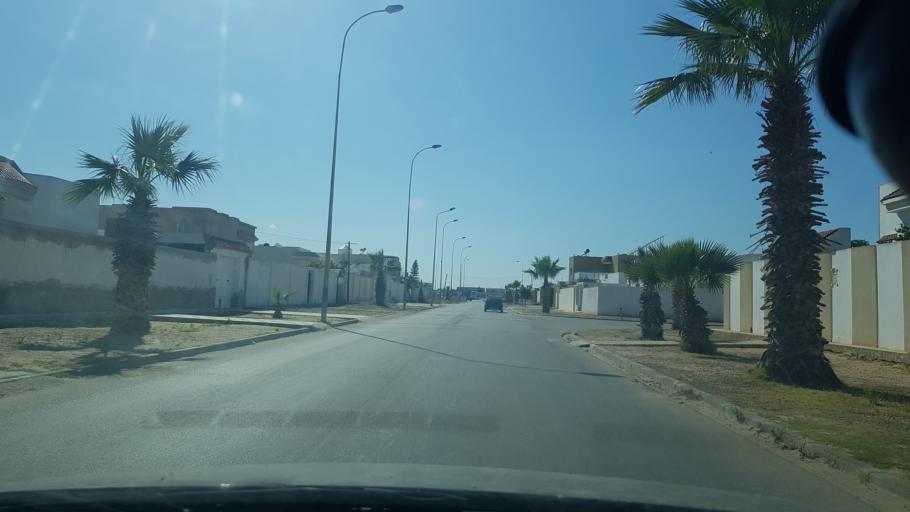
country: TN
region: Safaqis
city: Al Qarmadah
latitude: 34.8276
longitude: 10.7557
